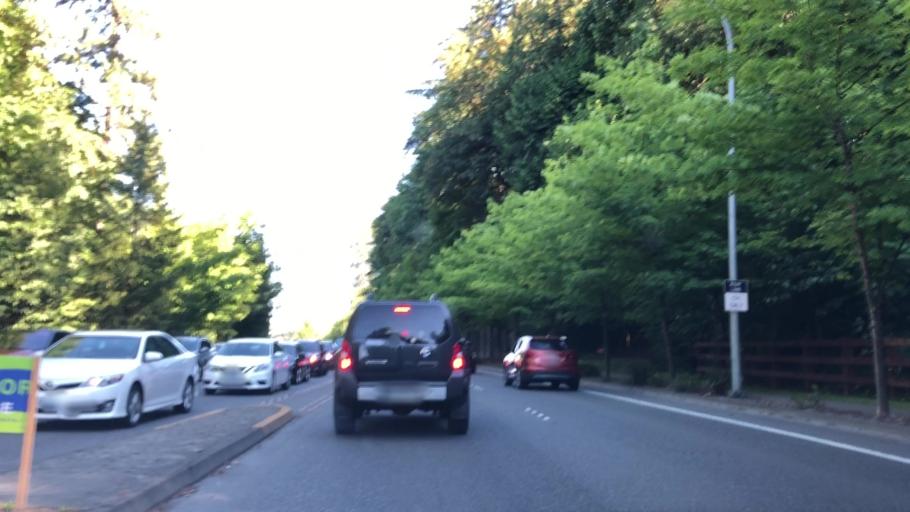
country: US
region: Washington
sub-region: King County
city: Redmond
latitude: 47.6613
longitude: -122.1258
